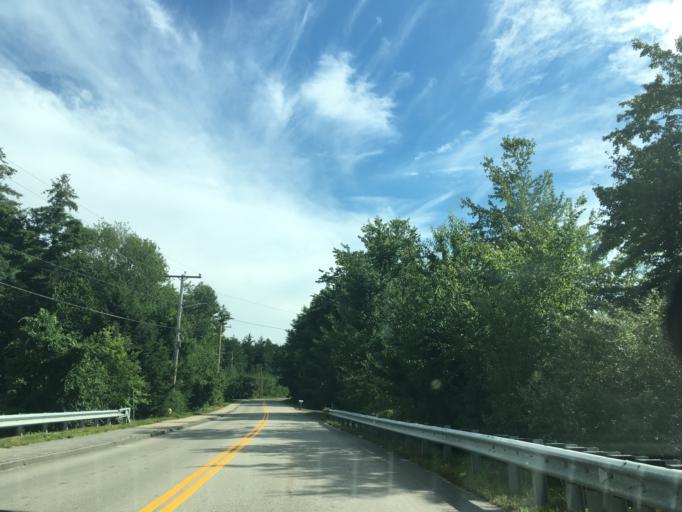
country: US
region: New Hampshire
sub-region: Rockingham County
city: Exeter
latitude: 42.9720
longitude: -70.9597
